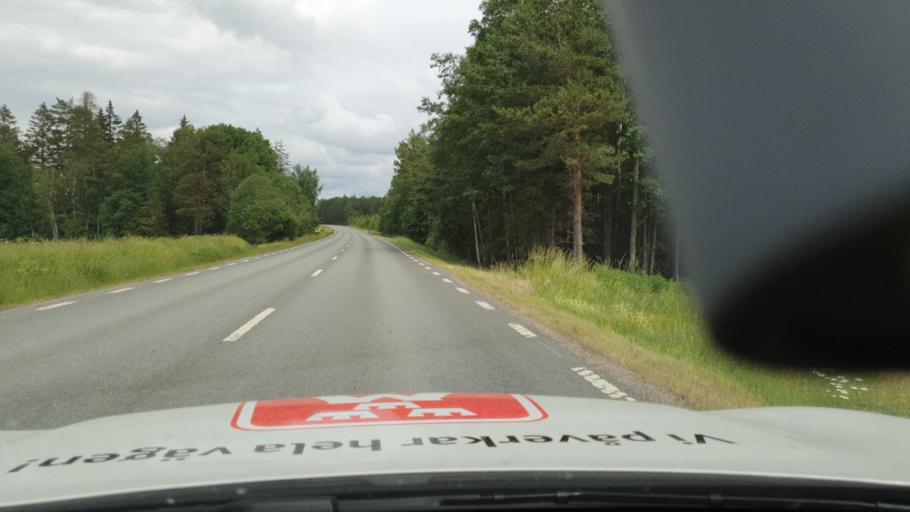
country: SE
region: Vaestra Goetaland
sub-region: Tidaholms Kommun
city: Olofstorp
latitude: 58.1981
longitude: 14.0387
